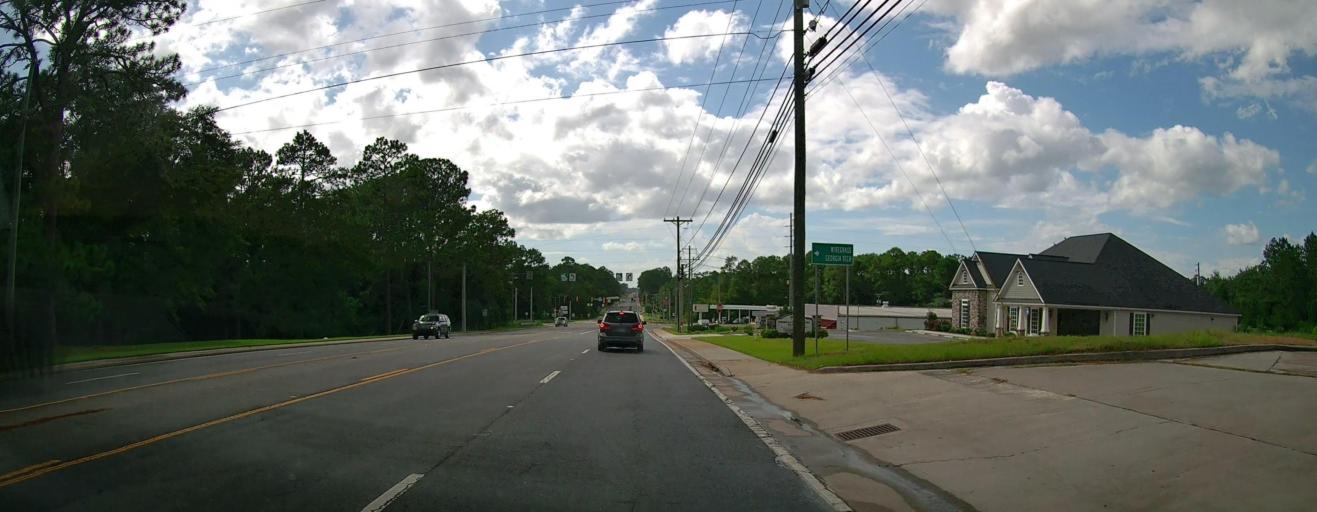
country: US
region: Georgia
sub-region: Coffee County
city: Douglas
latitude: 31.5118
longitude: -82.8690
